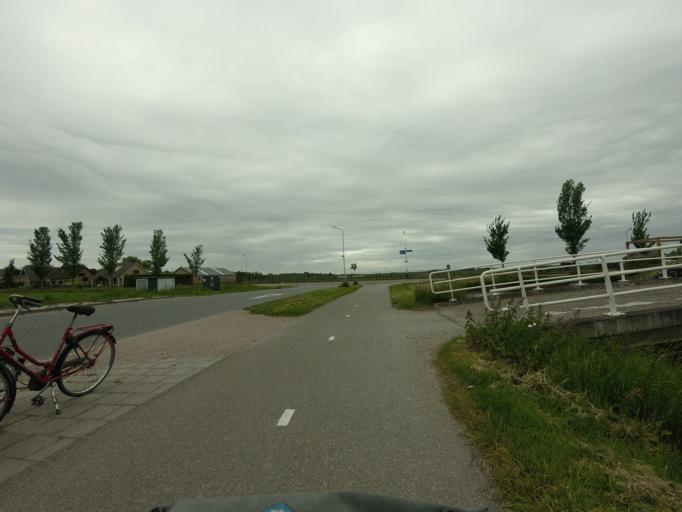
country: NL
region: North Holland
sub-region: Gemeente Medemblik
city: Opperdoes
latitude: 52.7541
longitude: 5.0758
